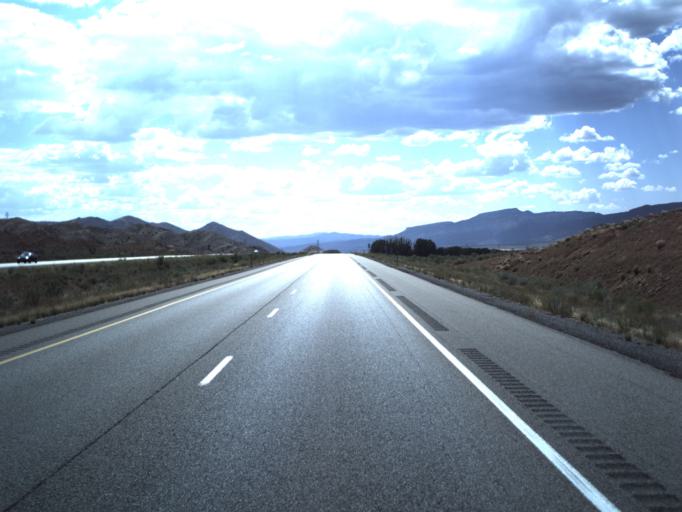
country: US
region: Utah
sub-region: Sevier County
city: Aurora
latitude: 38.9110
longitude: -111.8911
